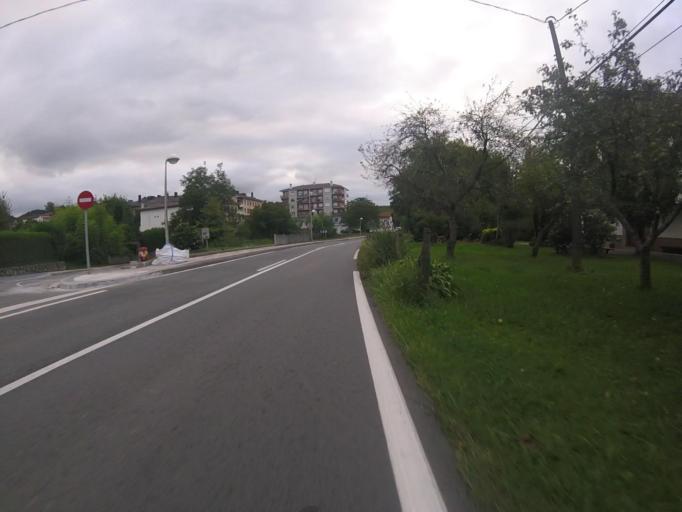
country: ES
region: Basque Country
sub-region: Provincia de Guipuzcoa
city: Errenteria
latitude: 43.2925
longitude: -1.8636
